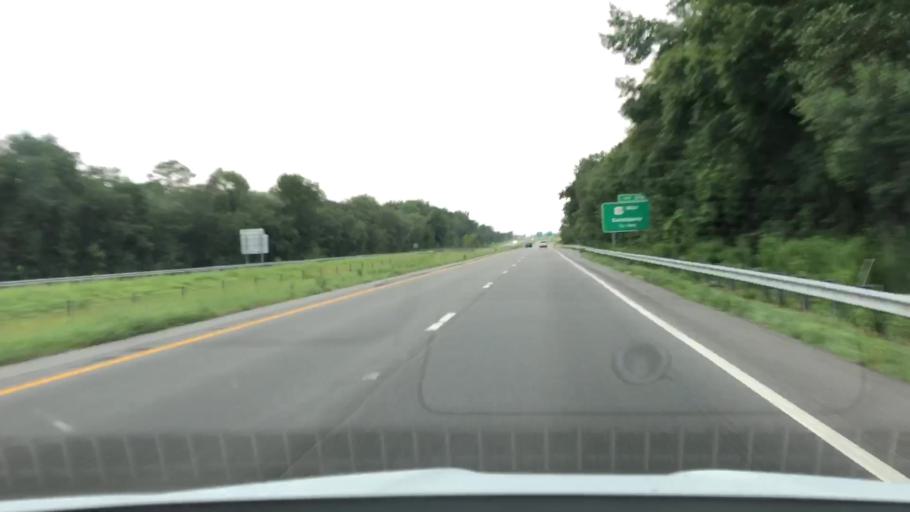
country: US
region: North Carolina
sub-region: Lenoir County
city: La Grange
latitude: 35.2955
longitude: -77.8053
